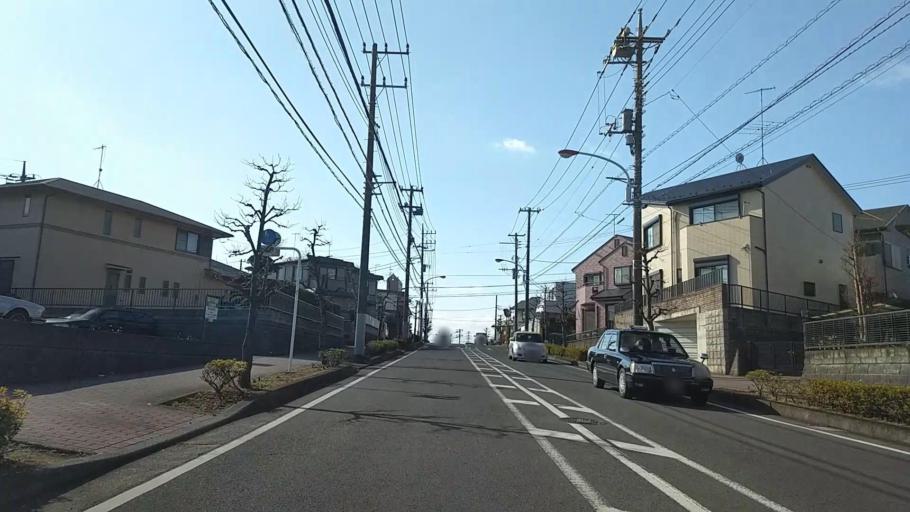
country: JP
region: Kanagawa
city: Isehara
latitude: 35.3946
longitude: 139.3049
